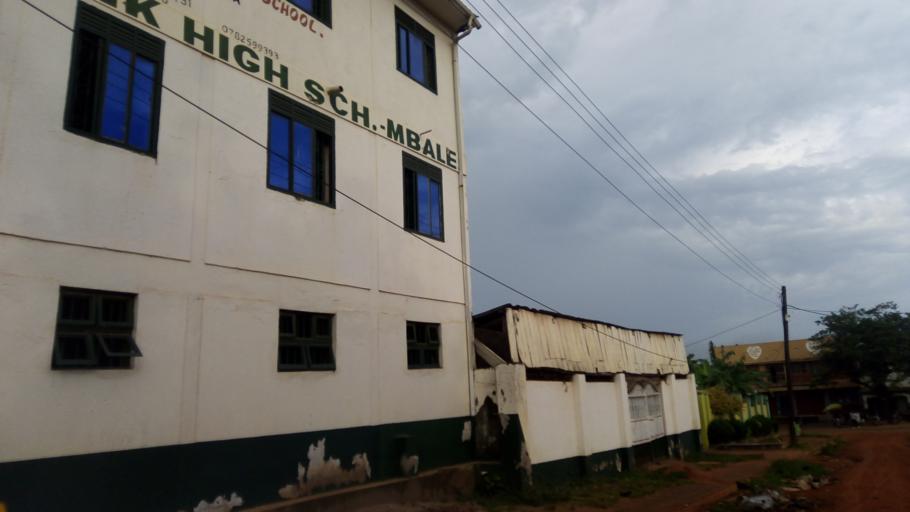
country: UG
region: Eastern Region
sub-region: Mbale District
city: Mbale
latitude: 1.0779
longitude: 34.1697
